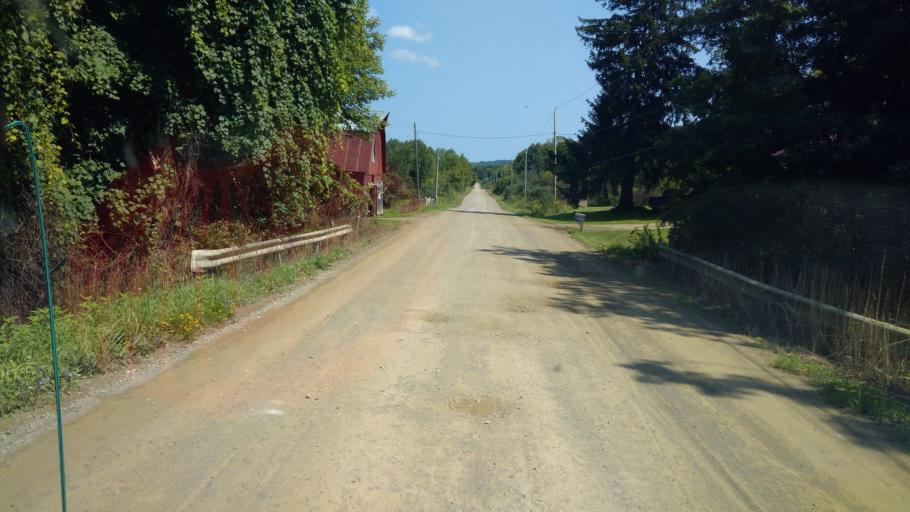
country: US
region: New York
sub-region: Allegany County
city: Houghton
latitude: 42.3535
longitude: -78.0587
